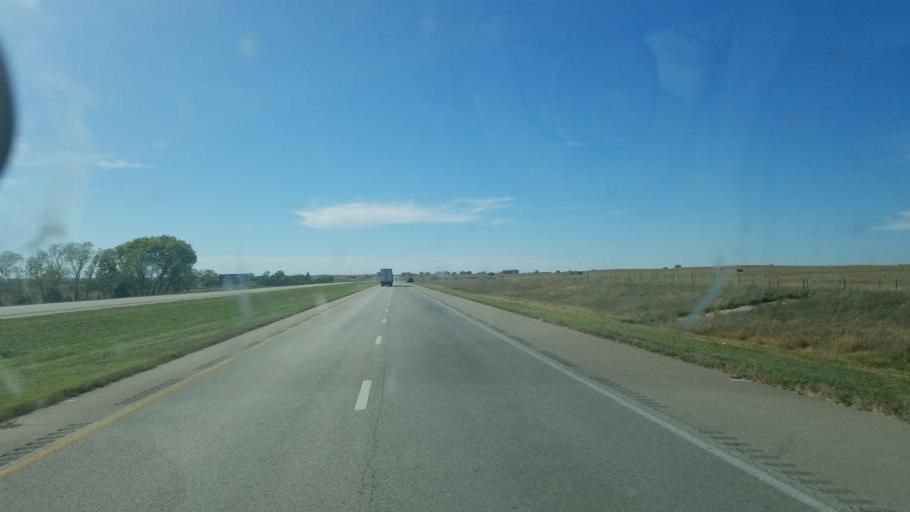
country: US
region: Kansas
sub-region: Saline County
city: Salina
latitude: 38.8783
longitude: -97.6929
